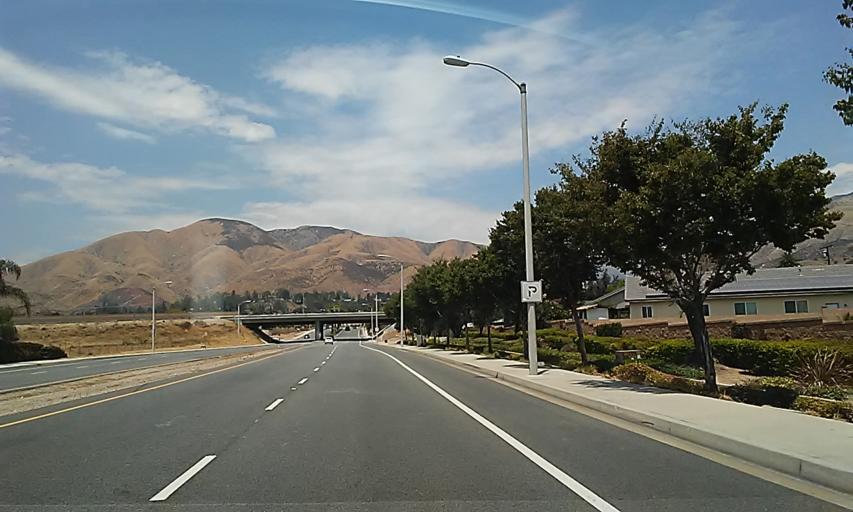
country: US
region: California
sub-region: San Bernardino County
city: Highland
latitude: 34.1306
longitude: -117.1954
